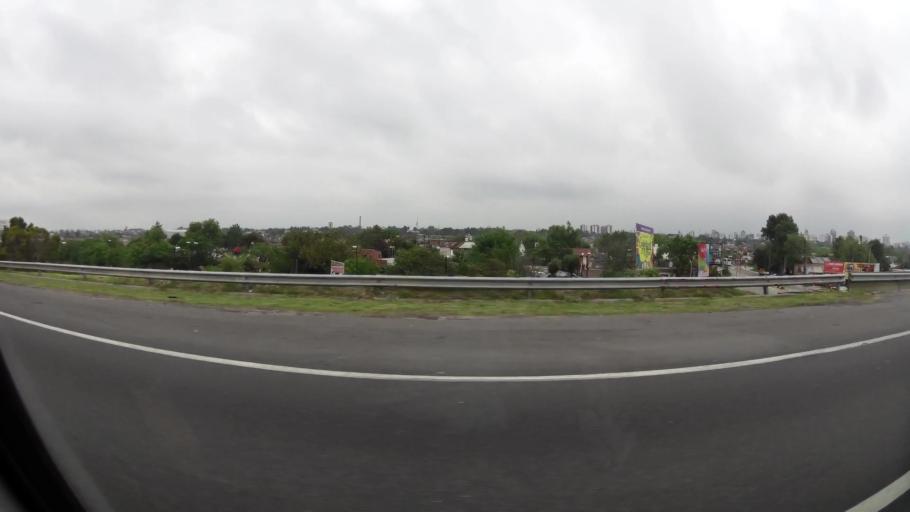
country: AR
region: Buenos Aires
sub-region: Partido de Quilmes
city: Quilmes
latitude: -34.7174
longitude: -58.2345
